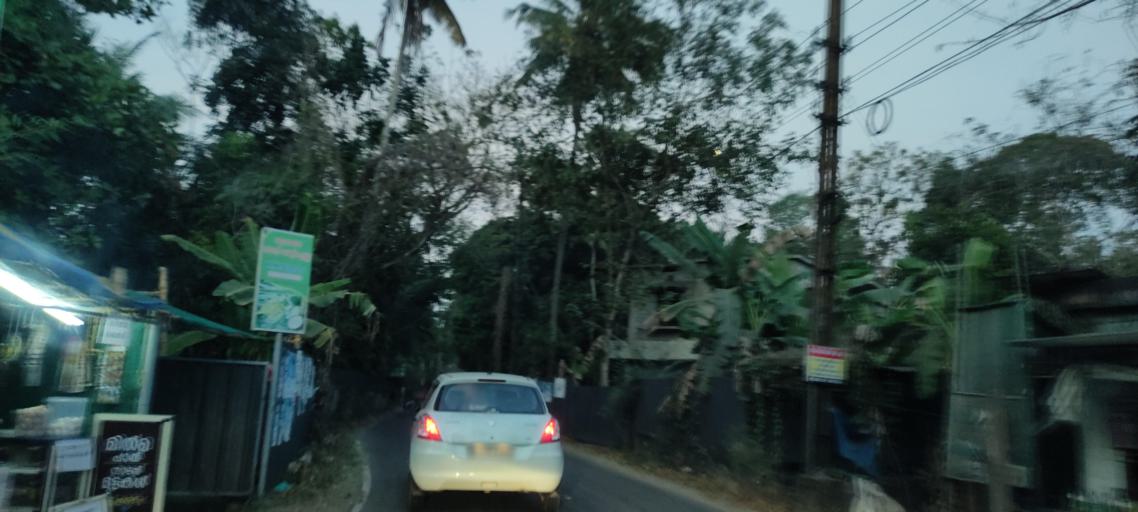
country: IN
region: Kerala
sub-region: Alappuzha
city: Kutiatodu
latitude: 9.7686
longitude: 76.3238
